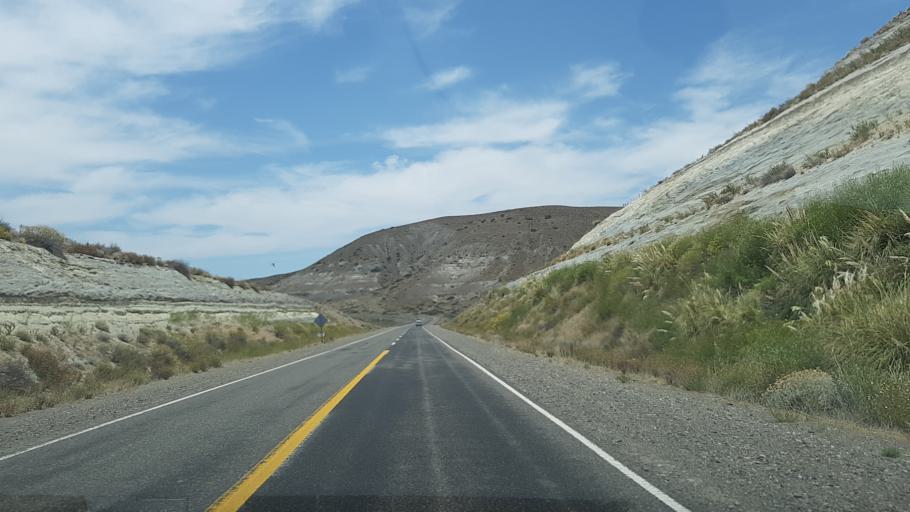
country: AR
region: Neuquen
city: Junin de los Andes
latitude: -40.4530
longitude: -70.6650
